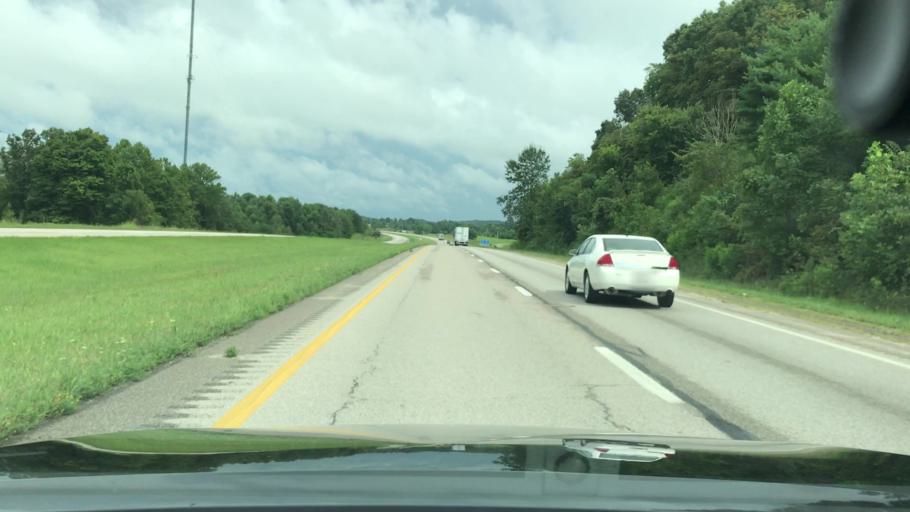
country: US
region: Ohio
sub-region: Gallia County
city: Gallipolis
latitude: 38.8872
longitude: -82.3482
